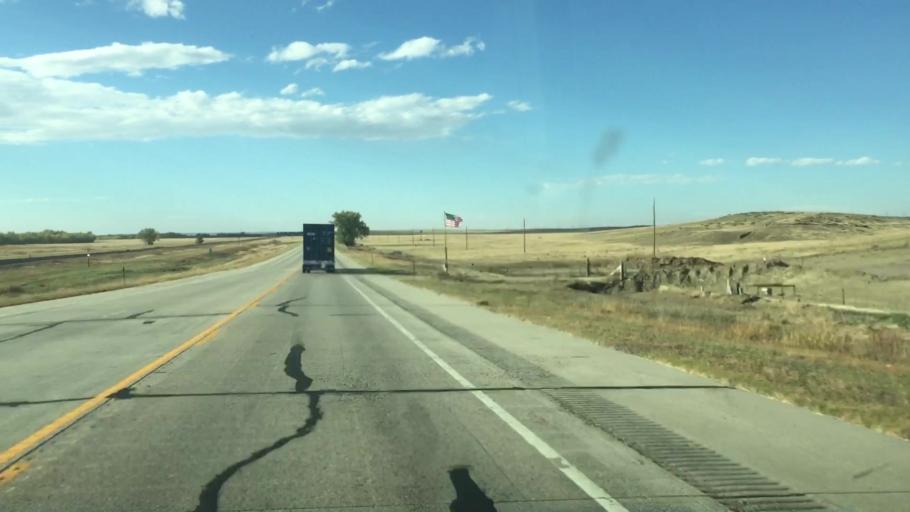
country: US
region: Colorado
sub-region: Lincoln County
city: Limon
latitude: 39.2158
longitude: -103.6026
